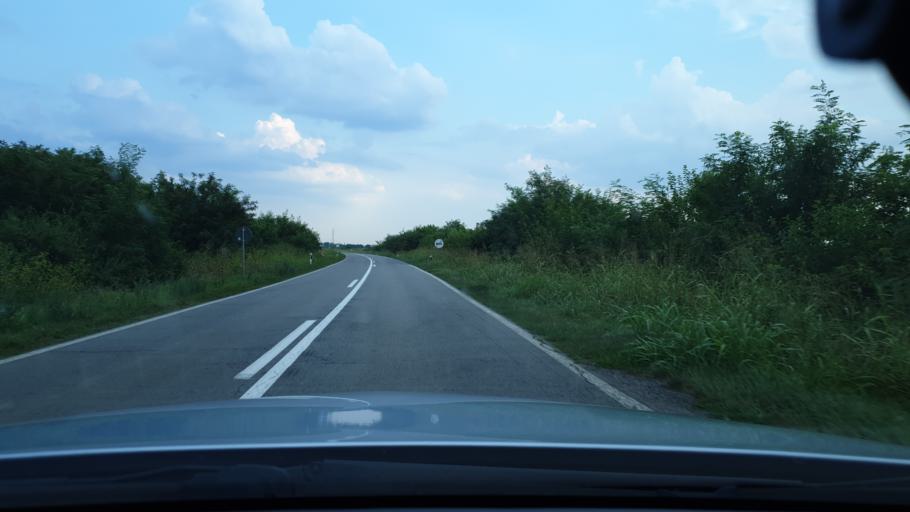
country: RS
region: Autonomna Pokrajina Vojvodina
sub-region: Juznobanatski Okrug
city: Plandiste
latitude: 45.2489
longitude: 21.1022
